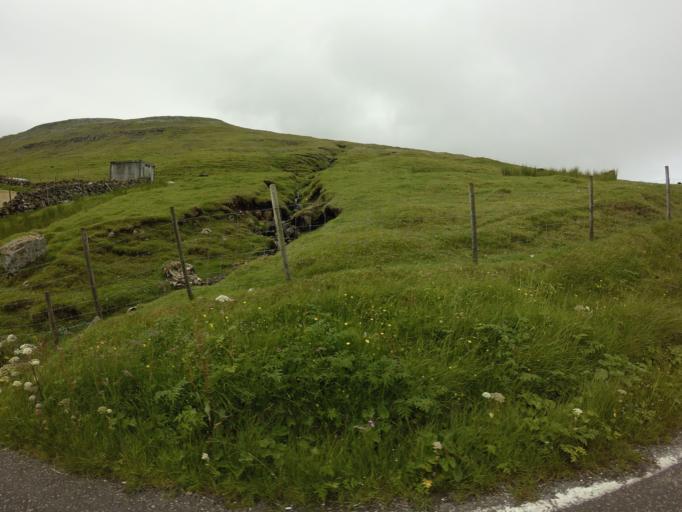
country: FO
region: Sandoy
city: Sandur
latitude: 61.8139
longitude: -6.6970
